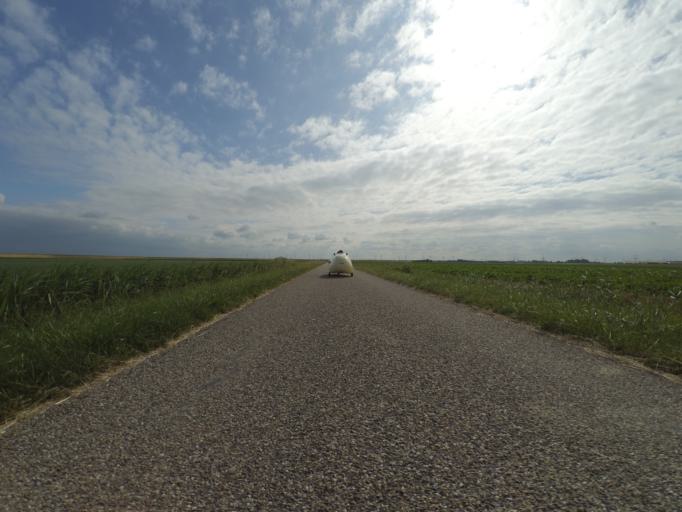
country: NL
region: Zeeland
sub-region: Gemeente Tholen
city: Tholen
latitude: 51.4348
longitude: 4.1709
